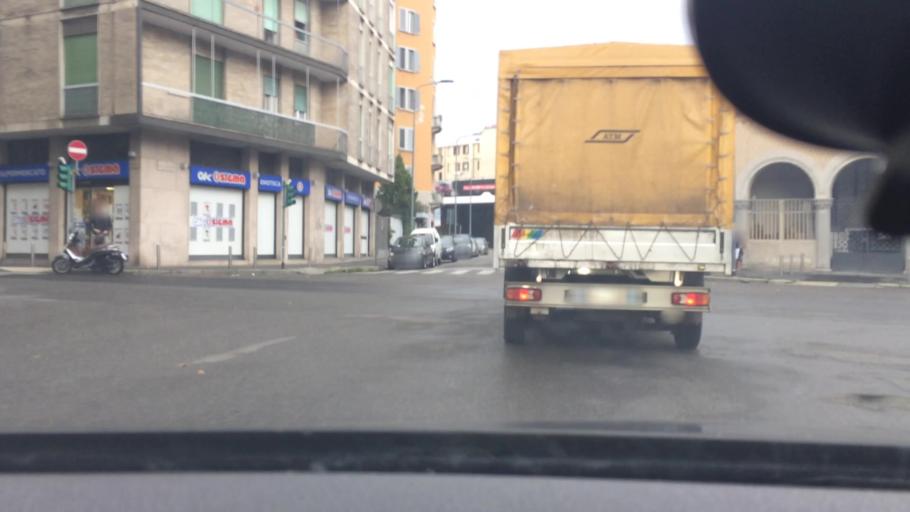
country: IT
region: Lombardy
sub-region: Citta metropolitana di Milano
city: Sesto San Giovanni
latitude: 45.4960
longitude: 9.2207
